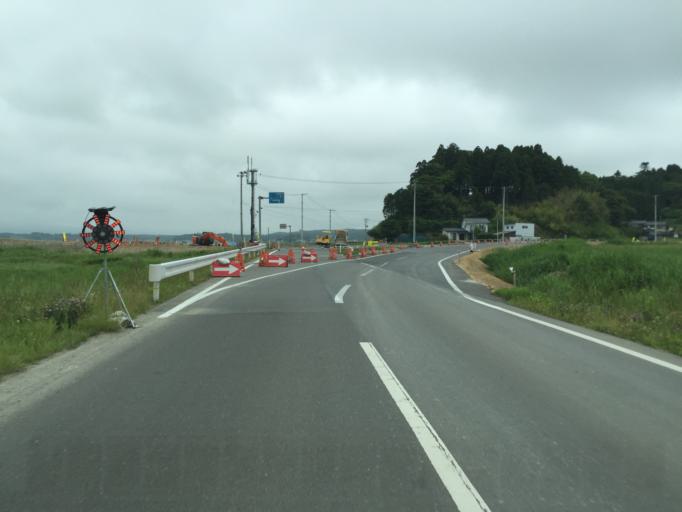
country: JP
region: Fukushima
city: Namie
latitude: 37.7265
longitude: 141.0052
